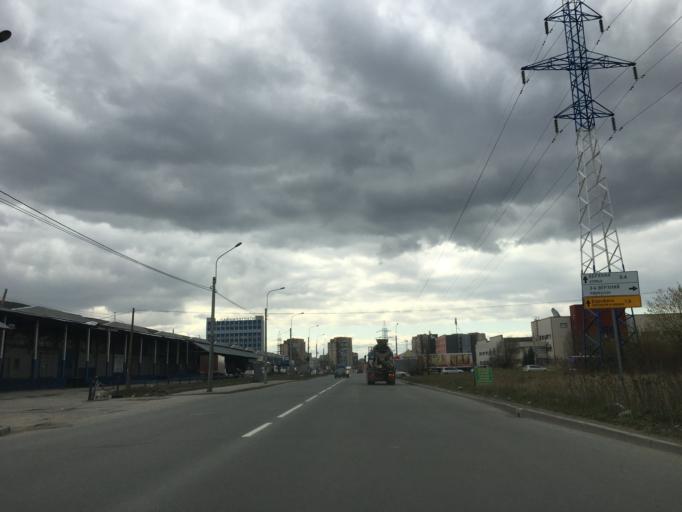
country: RU
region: Leningrad
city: Parnas
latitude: 60.0625
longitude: 30.3660
